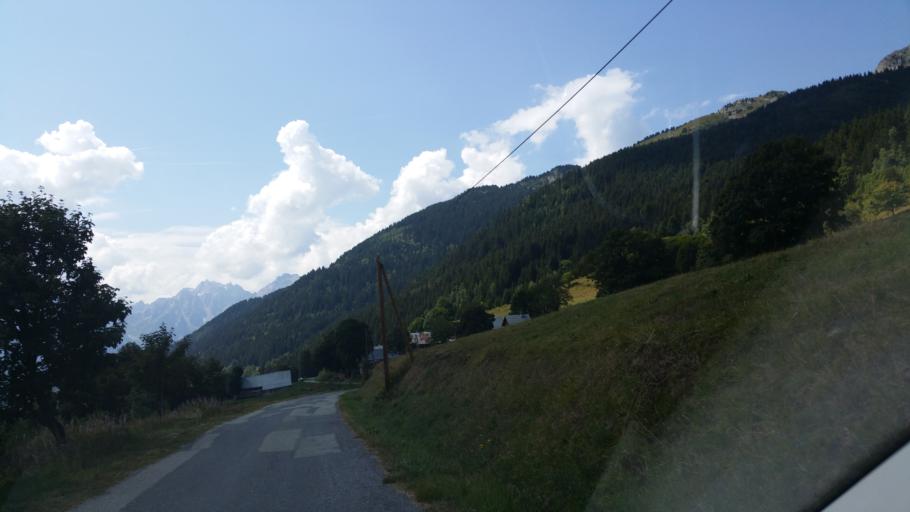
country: FR
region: Rhone-Alpes
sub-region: Departement de la Savoie
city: La Chambre
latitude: 45.4174
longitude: 6.3501
